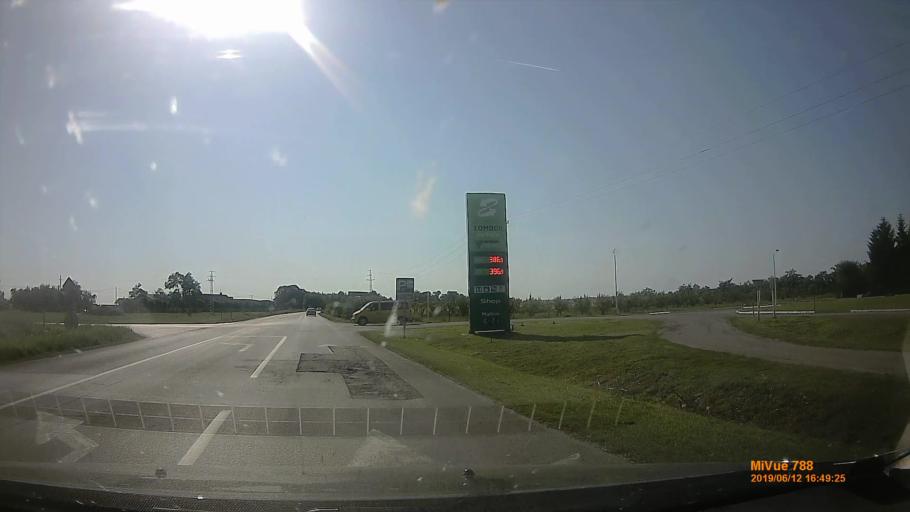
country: HU
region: Csongrad
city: Kiszombor
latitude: 46.1935
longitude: 20.4112
